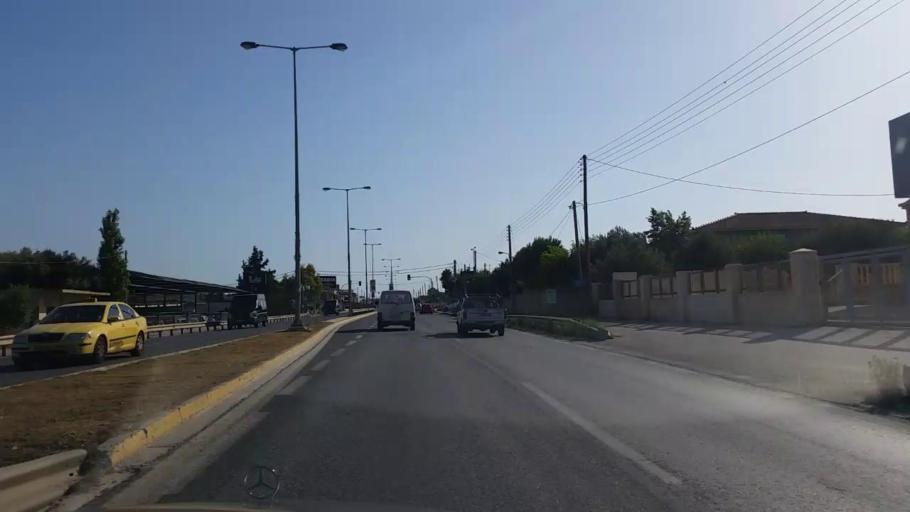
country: GR
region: Attica
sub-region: Nomarchia Anatolikis Attikis
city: Kitsi
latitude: 37.8722
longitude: 23.8592
